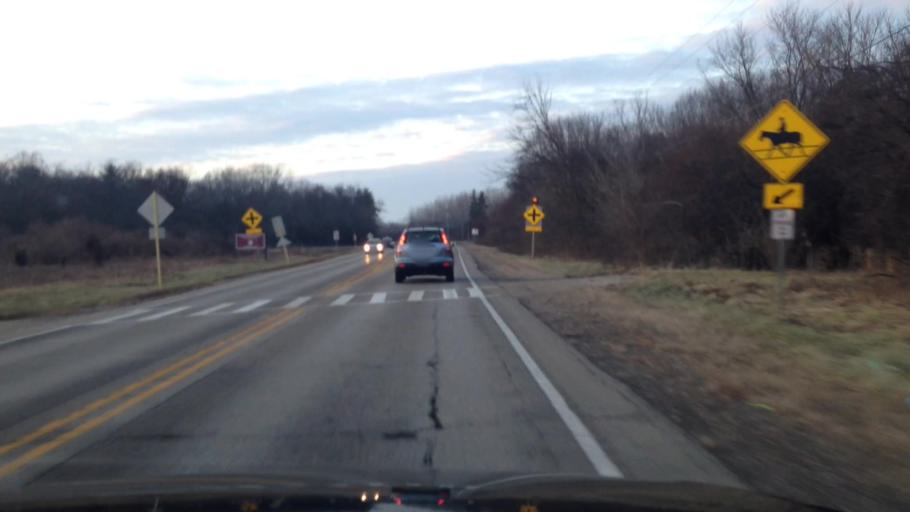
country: US
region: Illinois
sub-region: Kane County
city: Carpentersville
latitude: 42.1289
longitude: -88.2214
